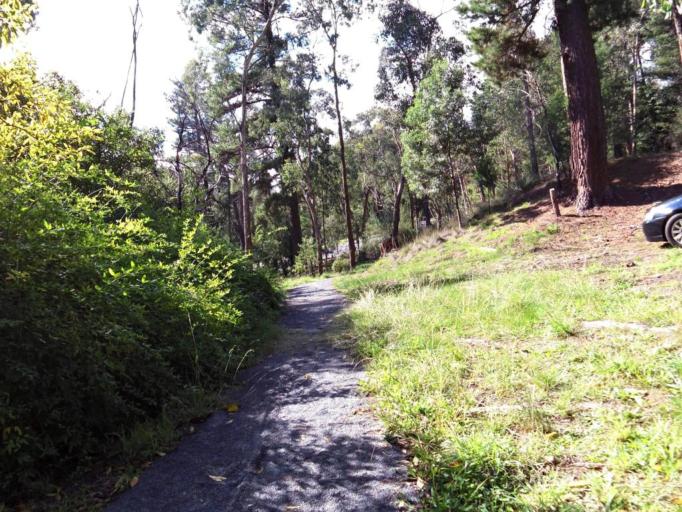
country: AU
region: Victoria
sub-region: Yarra Ranges
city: Mount Evelyn
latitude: -37.7818
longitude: 145.3674
